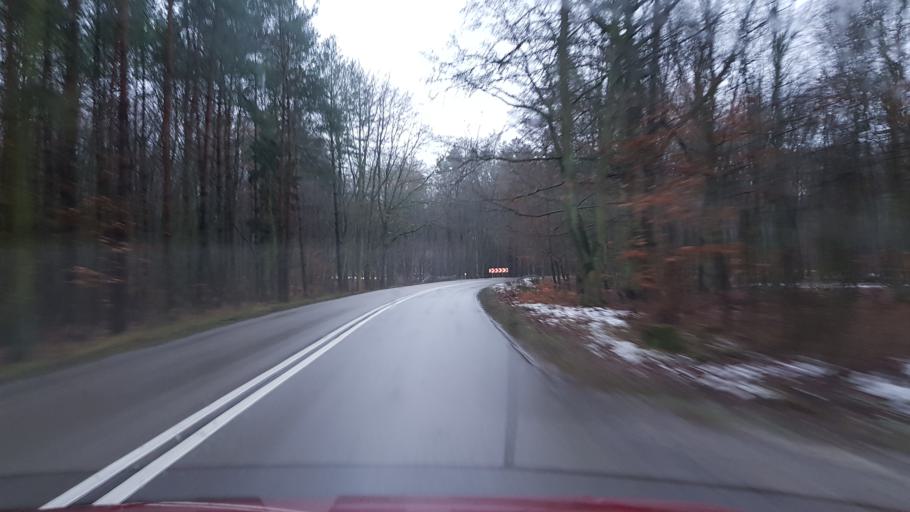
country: PL
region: West Pomeranian Voivodeship
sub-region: Powiat policki
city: Police
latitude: 53.5237
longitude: 14.5264
